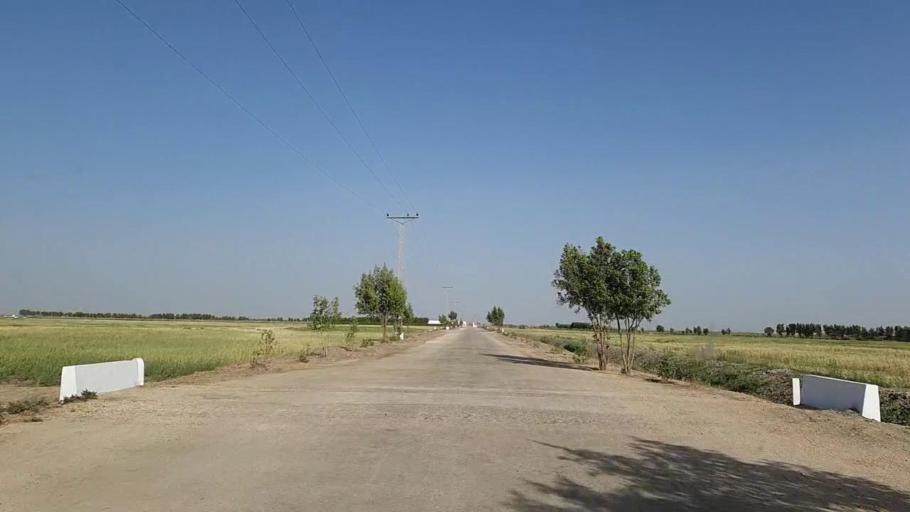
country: PK
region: Sindh
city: Jati
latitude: 24.5143
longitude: 68.1811
